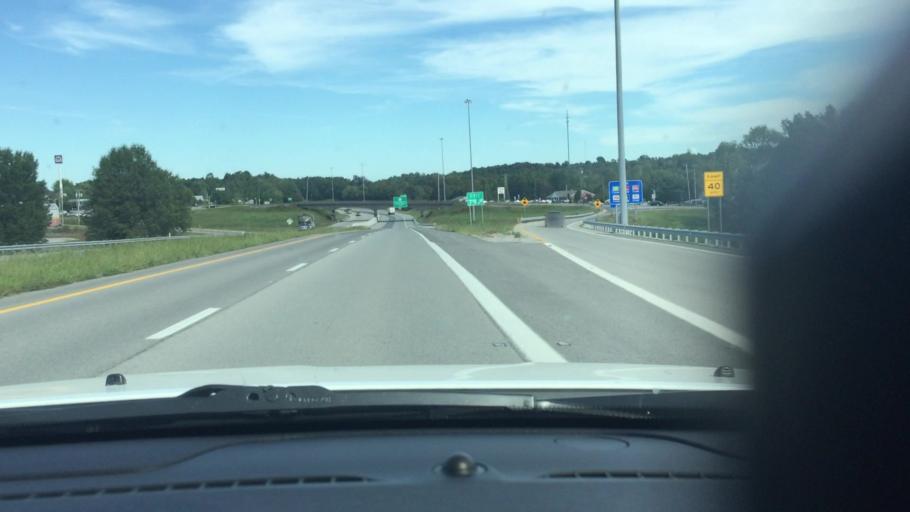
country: US
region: Kentucky
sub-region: Caldwell County
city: Princeton
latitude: 37.1216
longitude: -87.8973
